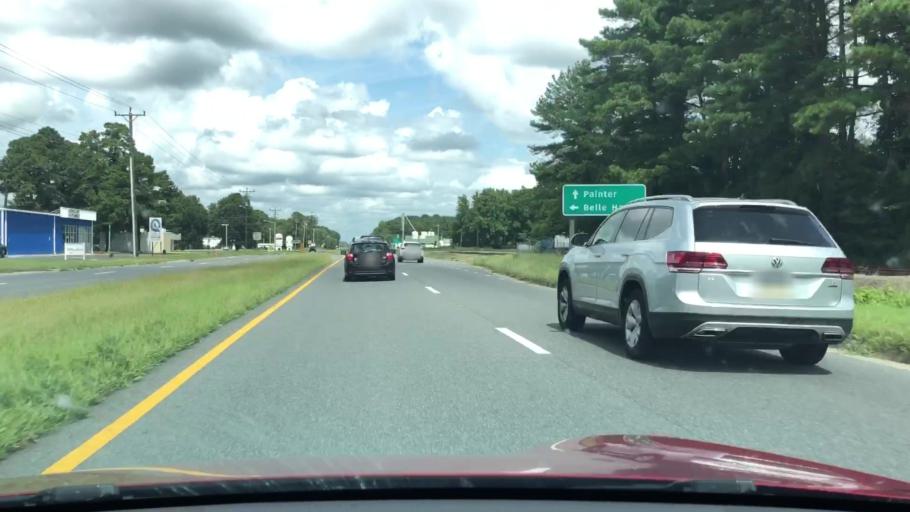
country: US
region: Virginia
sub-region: Northampton County
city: Exmore
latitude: 37.5482
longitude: -75.8126
